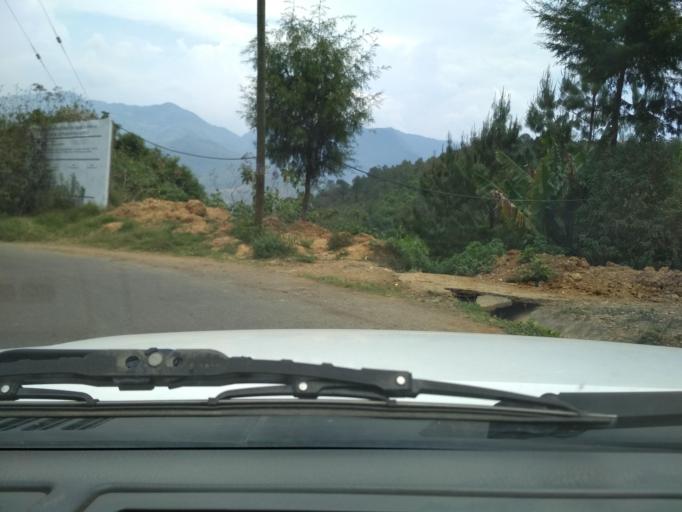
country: MX
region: Veracruz
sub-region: Camerino Z. Mendoza
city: La Cuesta
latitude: 18.7900
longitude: -97.1697
